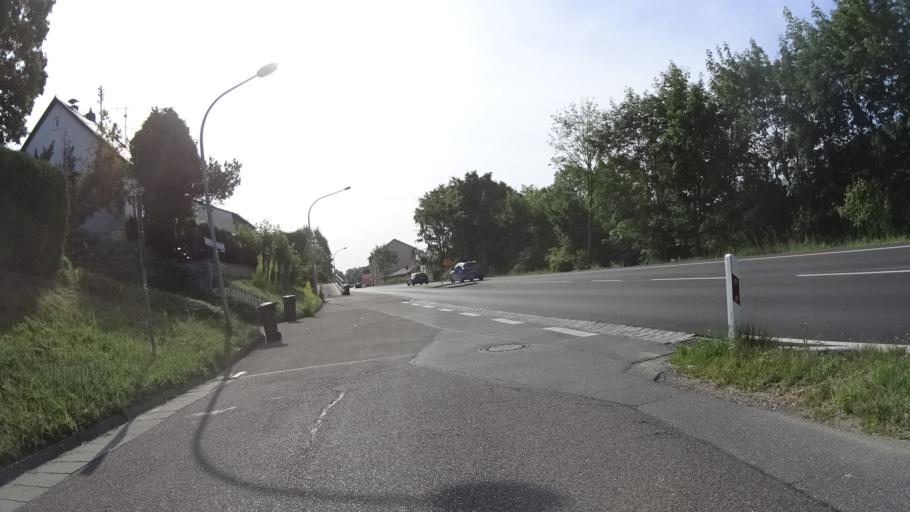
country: DE
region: Bavaria
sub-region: Lower Bavaria
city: Ihrlerstein
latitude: 48.9246
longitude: 11.8604
